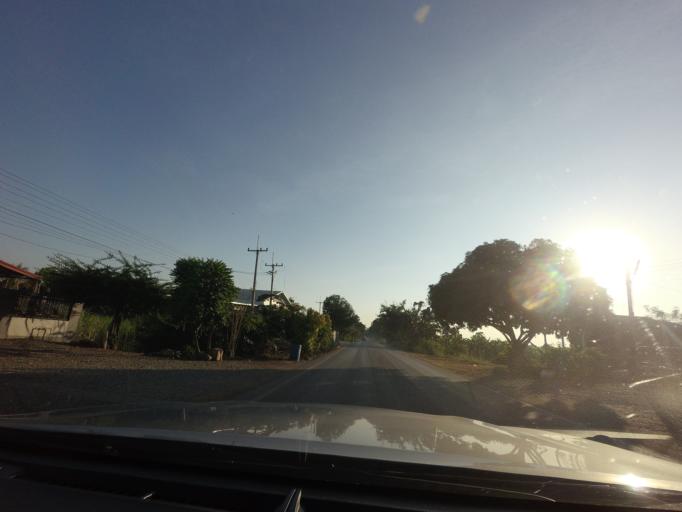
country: TH
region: Sukhothai
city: Sawankhalok
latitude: 17.3904
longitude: 99.7942
